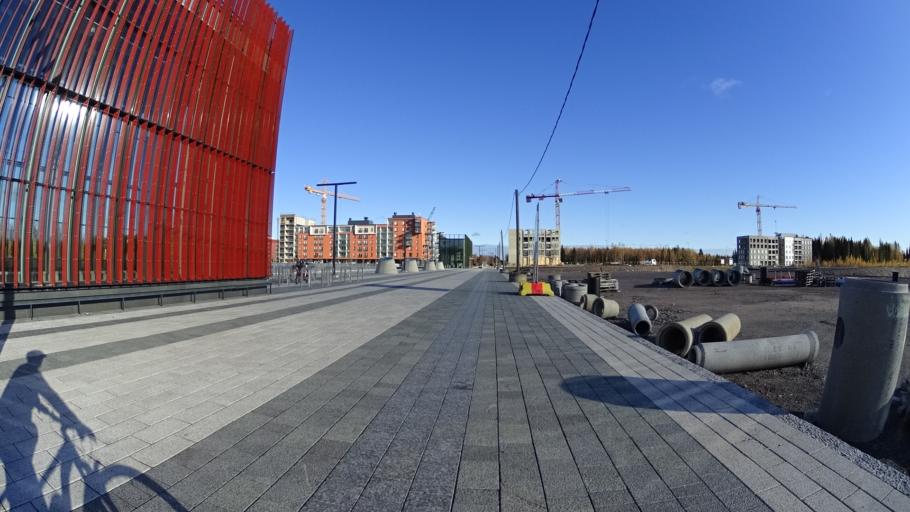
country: FI
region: Uusimaa
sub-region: Helsinki
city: Kilo
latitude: 60.3145
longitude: 24.8473
